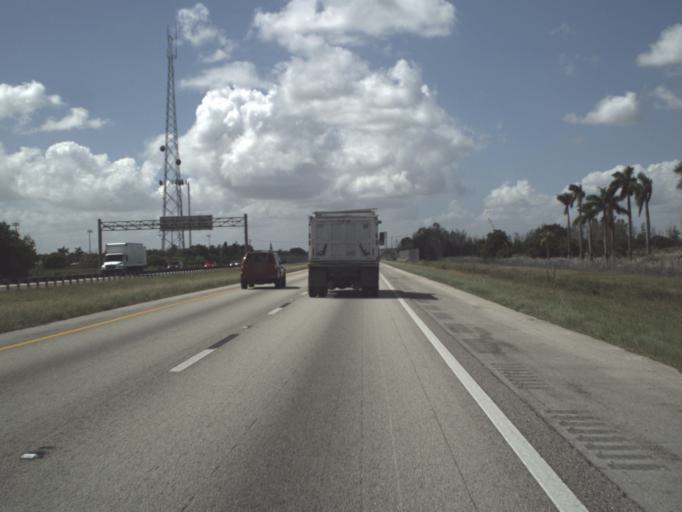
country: US
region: Florida
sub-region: Miami-Dade County
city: Country Club
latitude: 25.9614
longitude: -80.3361
